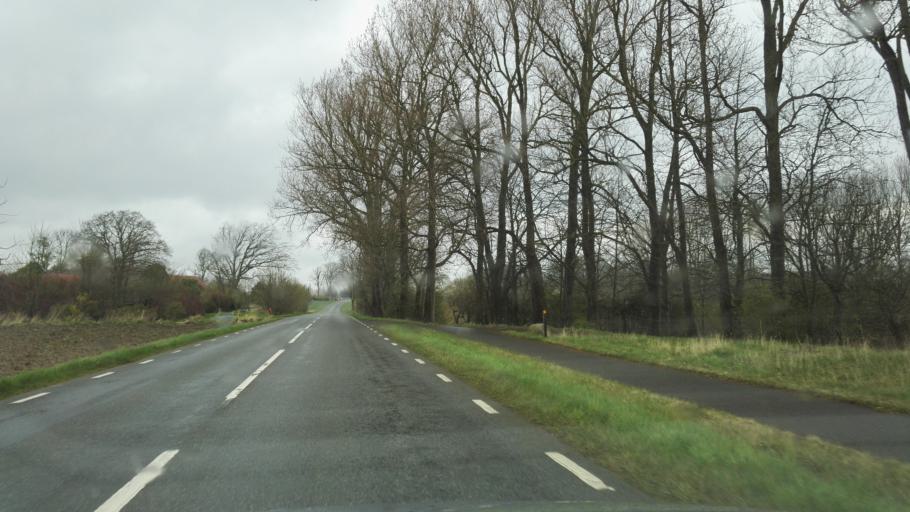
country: SE
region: Skane
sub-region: Simrishamns Kommun
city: Simrishamn
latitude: 55.4989
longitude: 14.3197
